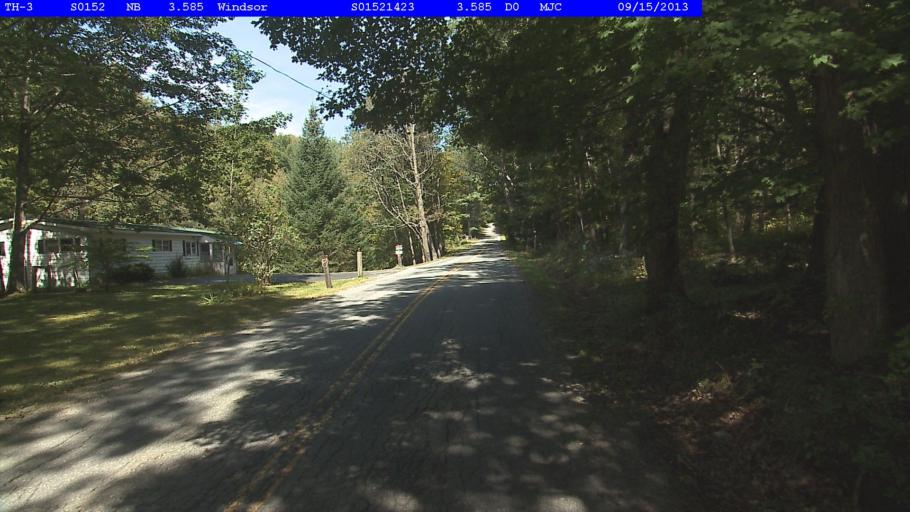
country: US
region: Vermont
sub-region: Windsor County
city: Windsor
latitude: 43.5123
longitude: -72.4345
